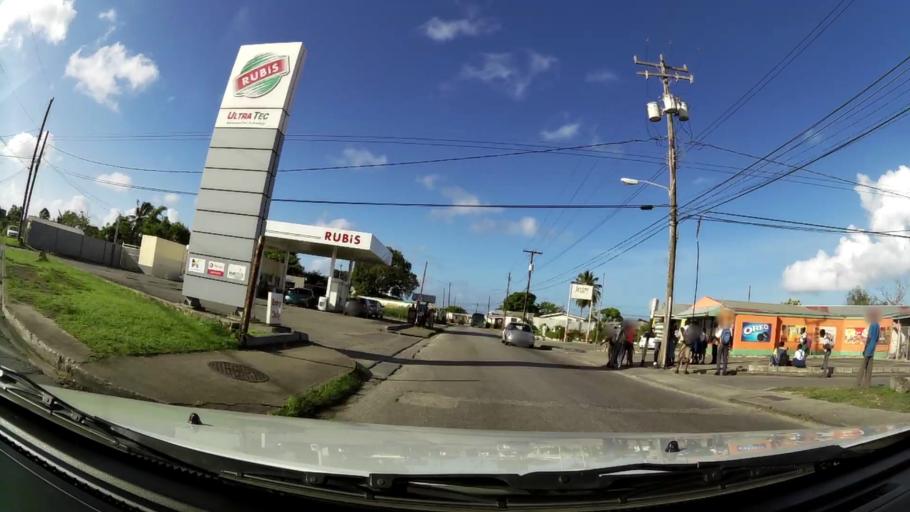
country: BB
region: Saint Michael
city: Bridgetown
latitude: 13.1084
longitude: -59.5949
